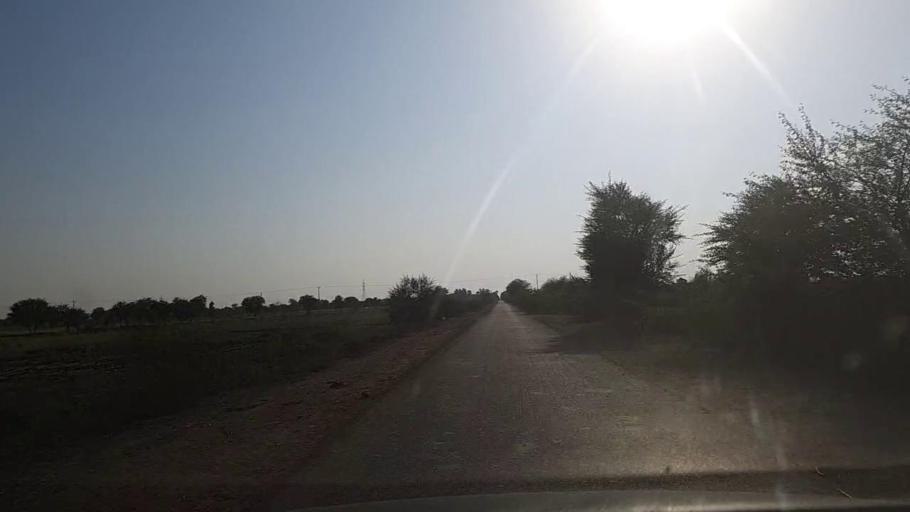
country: PK
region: Sindh
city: Naukot
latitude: 25.0018
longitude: 69.2696
